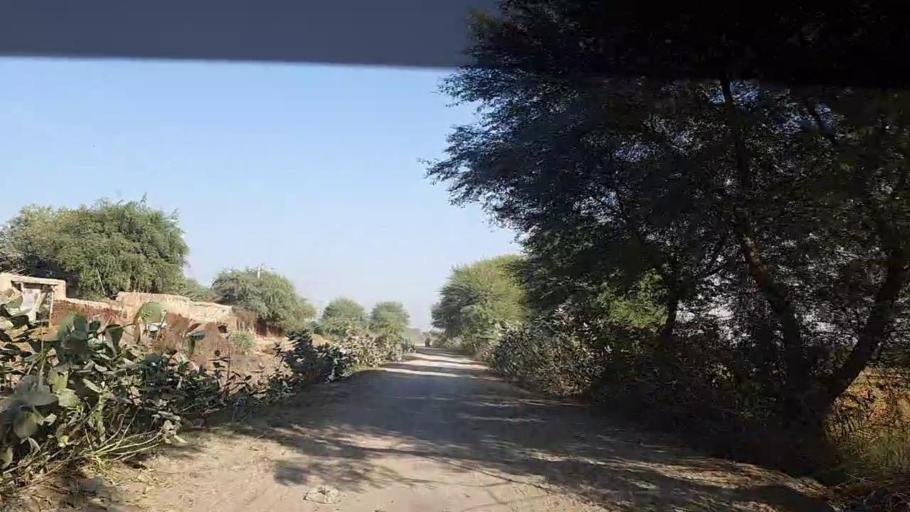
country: PK
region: Sindh
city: Larkana
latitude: 27.6264
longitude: 68.2565
